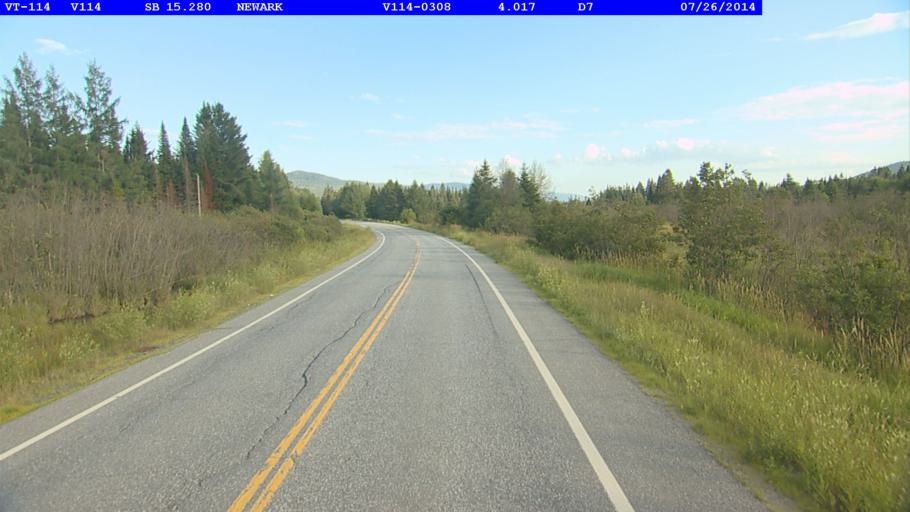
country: US
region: Vermont
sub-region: Caledonia County
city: Lyndonville
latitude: 44.7238
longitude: -71.8737
